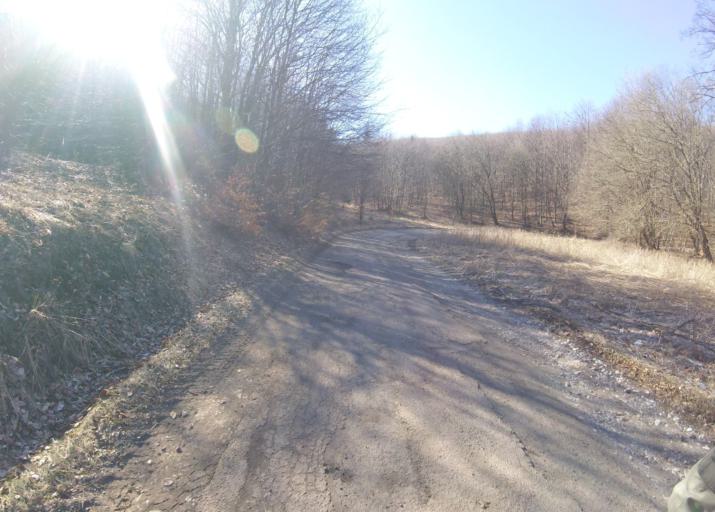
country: HU
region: Heves
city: Szilvasvarad
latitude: 48.0730
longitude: 20.4787
